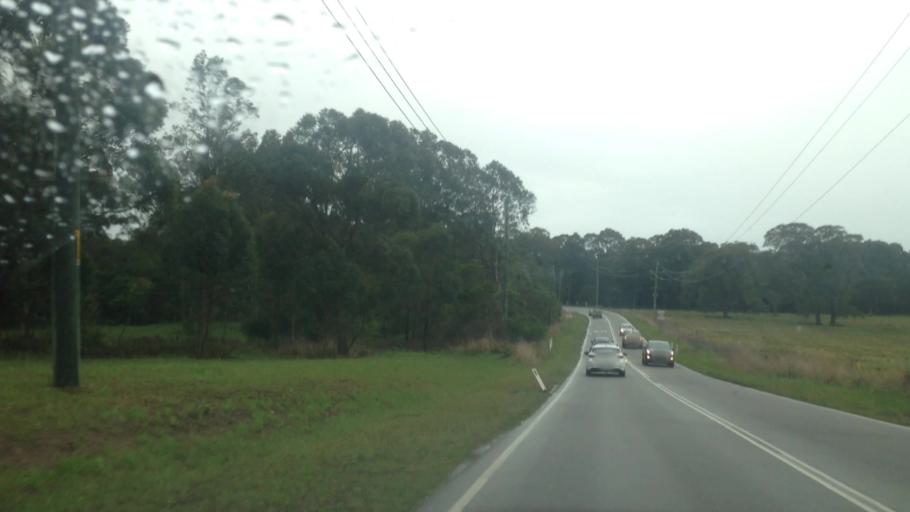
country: AU
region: New South Wales
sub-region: Wyong Shire
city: Charmhaven
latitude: -33.1663
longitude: 151.4767
